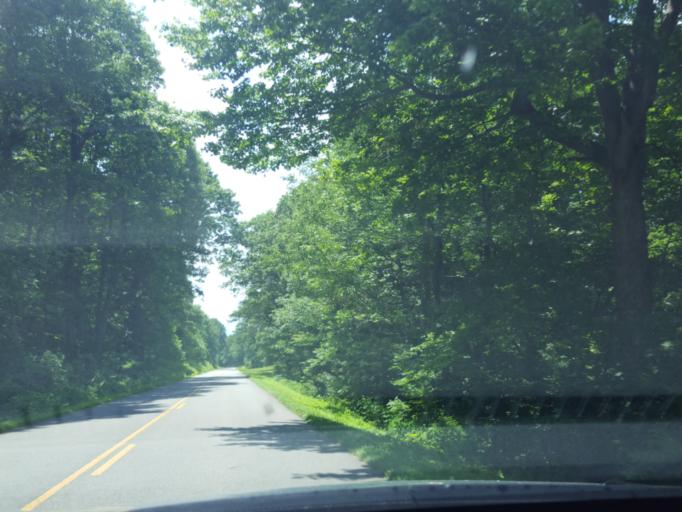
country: US
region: Virginia
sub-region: Nelson County
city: Nellysford
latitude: 37.9321
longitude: -78.9538
